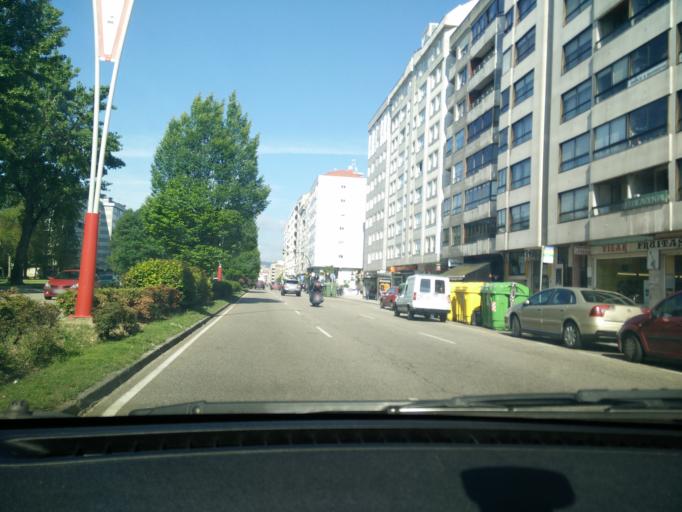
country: ES
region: Galicia
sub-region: Provincia de Pontevedra
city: Vigo
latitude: 42.2185
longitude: -8.7430
